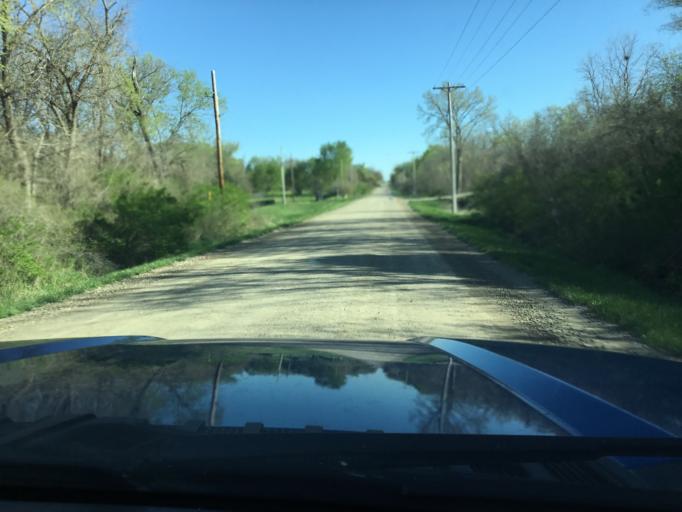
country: US
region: Kansas
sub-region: Douglas County
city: Lawrence
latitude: 38.9743
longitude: -95.3538
